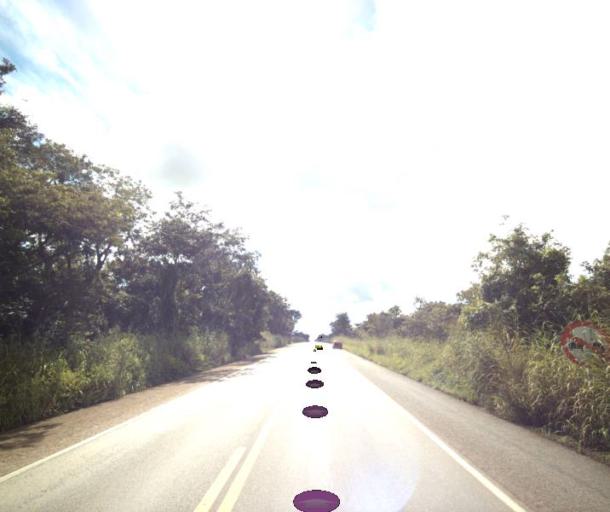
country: BR
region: Goias
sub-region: Jaragua
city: Jaragua
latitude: -15.9233
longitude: -49.2139
